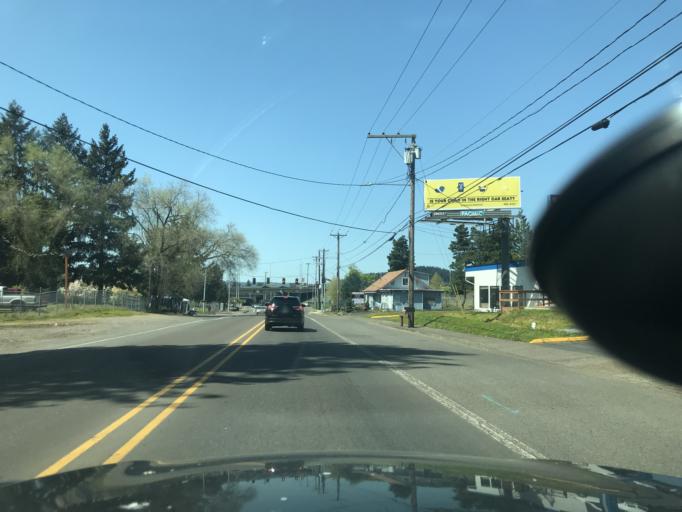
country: US
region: Oregon
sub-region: Multnomah County
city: Lents
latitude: 45.4965
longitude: -122.5619
